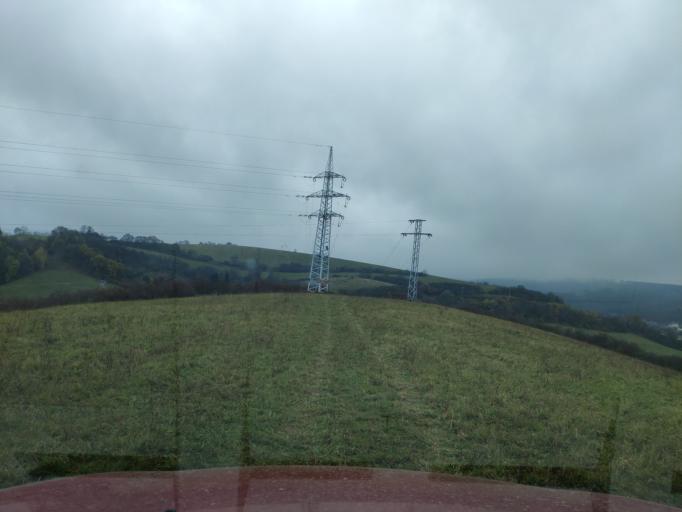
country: SK
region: Presovsky
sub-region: Okres Presov
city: Presov
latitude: 49.0027
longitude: 21.2085
